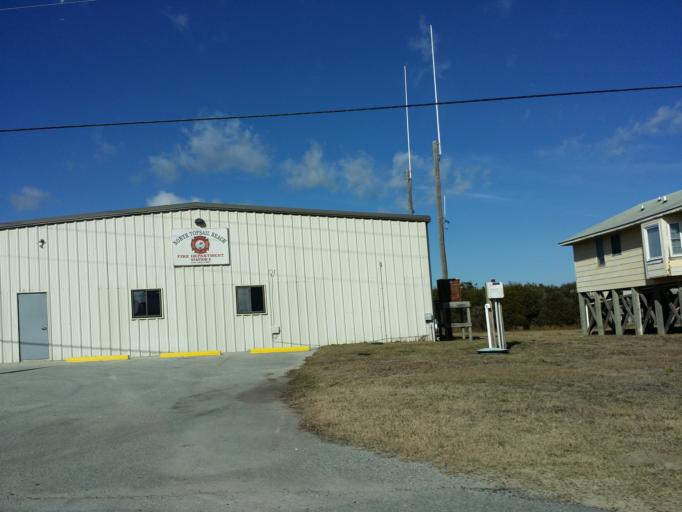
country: US
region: North Carolina
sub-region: Pender County
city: Surf City
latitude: 34.4575
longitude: -77.4923
